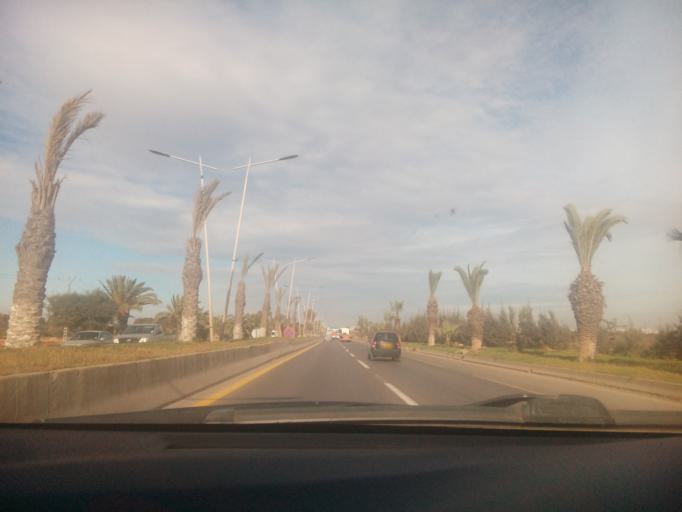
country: DZ
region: Oran
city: Es Senia
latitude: 35.6595
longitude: -0.5928
